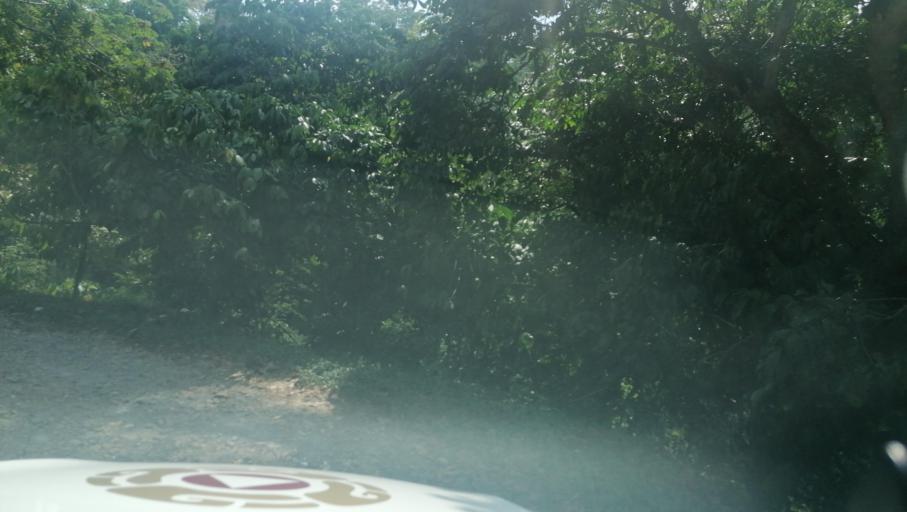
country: MX
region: Chiapas
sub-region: Cacahoatan
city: Benito Juarez
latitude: 15.0397
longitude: -92.2369
